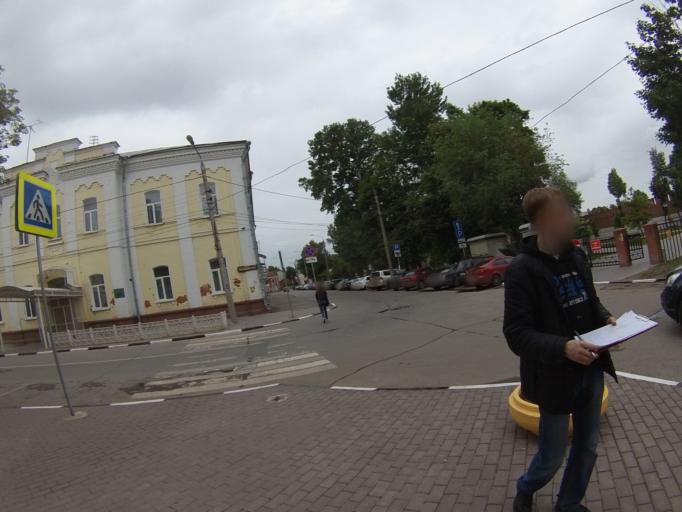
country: RU
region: Tula
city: Tula
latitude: 54.1935
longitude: 37.6232
